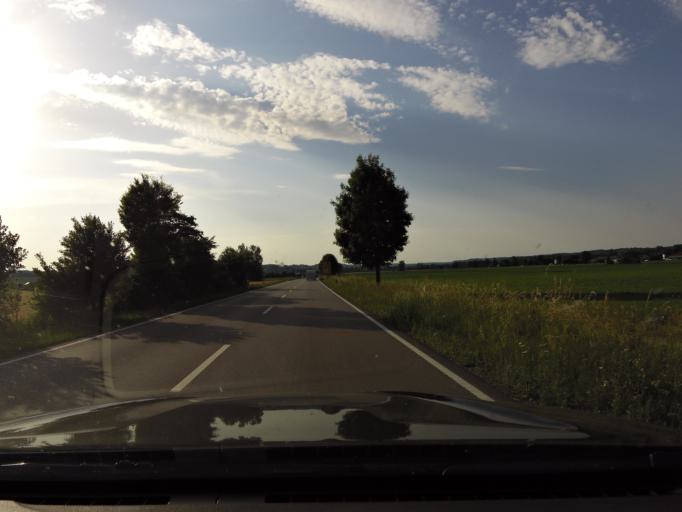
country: DE
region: Bavaria
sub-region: Upper Bavaria
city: Fridolfing
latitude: 48.0288
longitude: 12.7989
